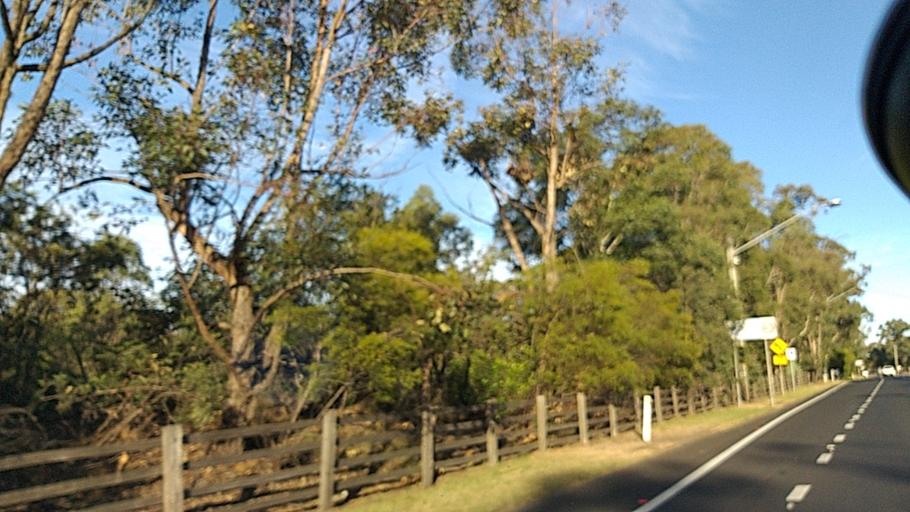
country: AU
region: New South Wales
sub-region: Hawkesbury
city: South Windsor
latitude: -33.6580
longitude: 150.7955
